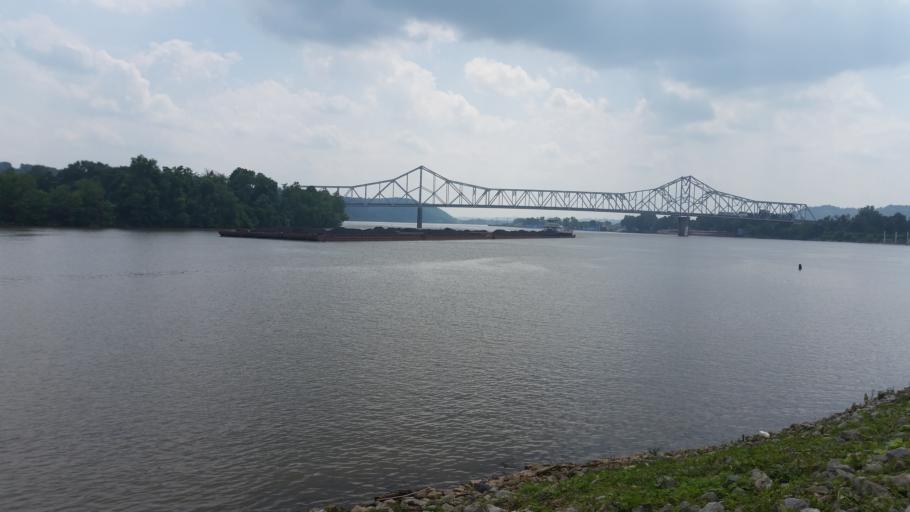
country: US
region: West Virginia
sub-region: Mason County
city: Point Pleasant
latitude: 38.8389
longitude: -82.1404
